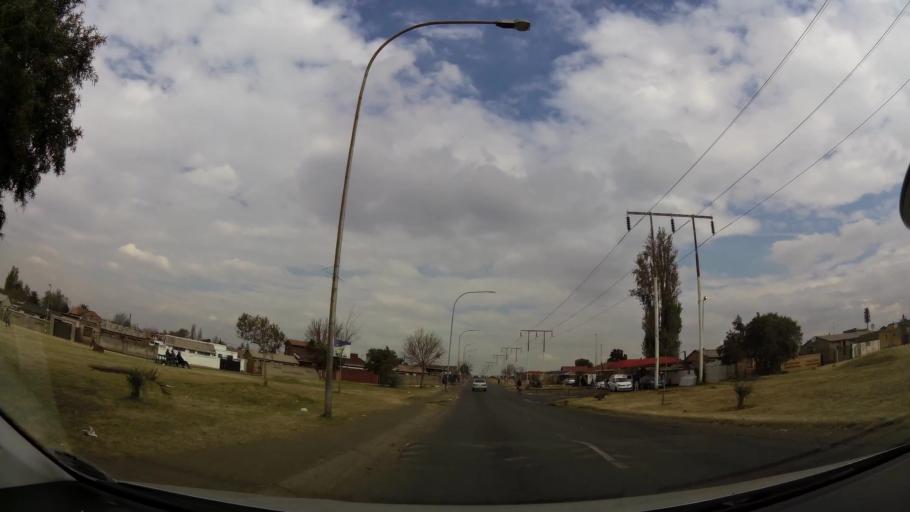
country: ZA
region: Gauteng
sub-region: City of Johannesburg Metropolitan Municipality
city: Soweto
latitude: -26.2701
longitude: 27.8606
